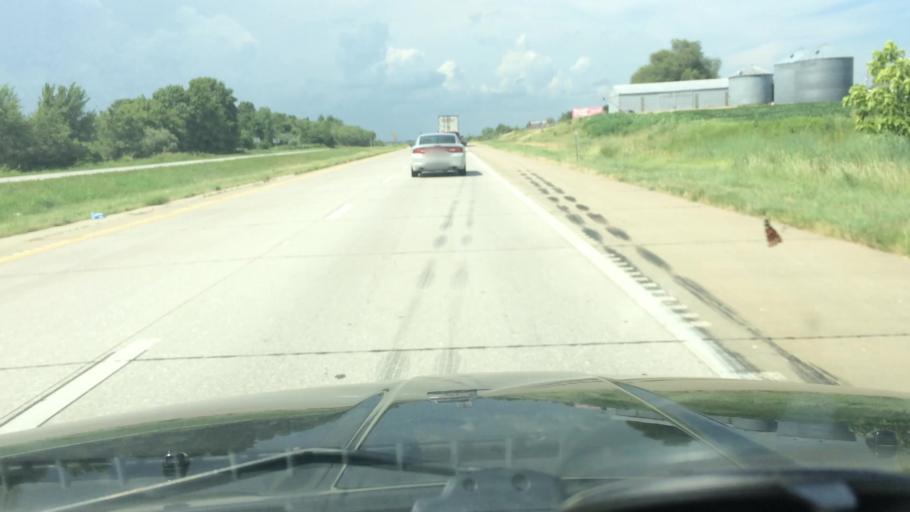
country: US
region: Missouri
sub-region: Henry County
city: Clinton
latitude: 38.3060
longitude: -93.7583
